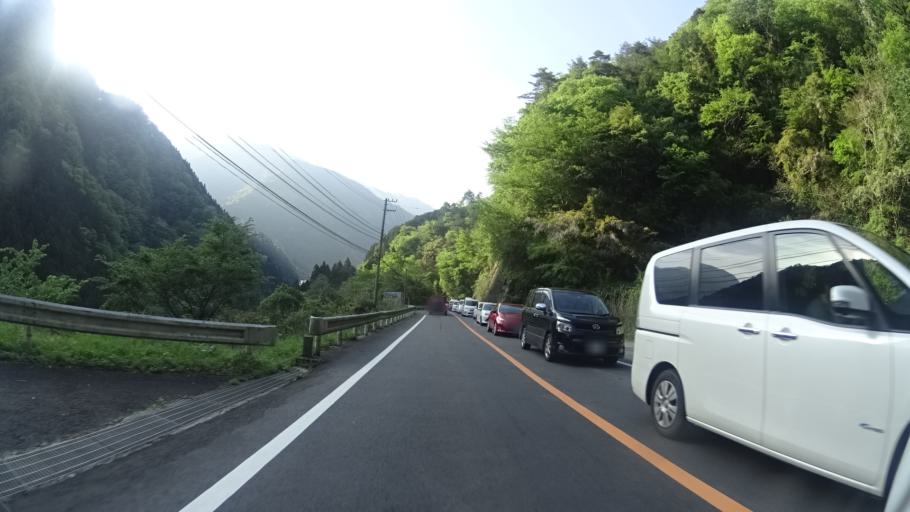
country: JP
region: Tokushima
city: Ikedacho
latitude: 33.8859
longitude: 133.8203
